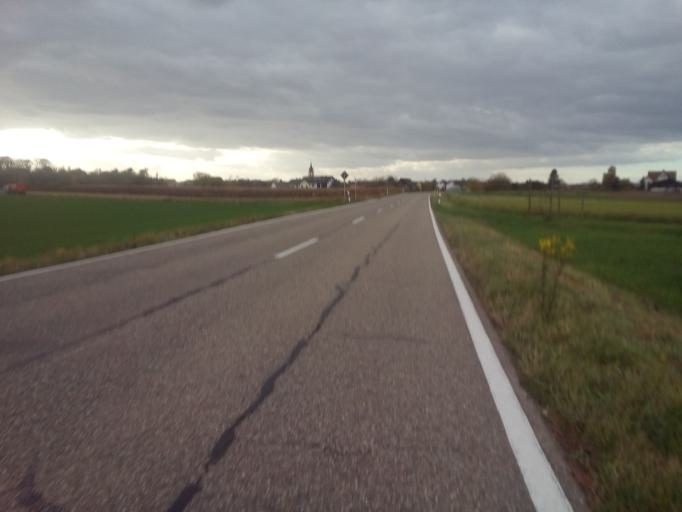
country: DE
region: Baden-Wuerttemberg
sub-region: Karlsruhe Region
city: Schwarzach
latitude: 48.7638
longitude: 8.0614
